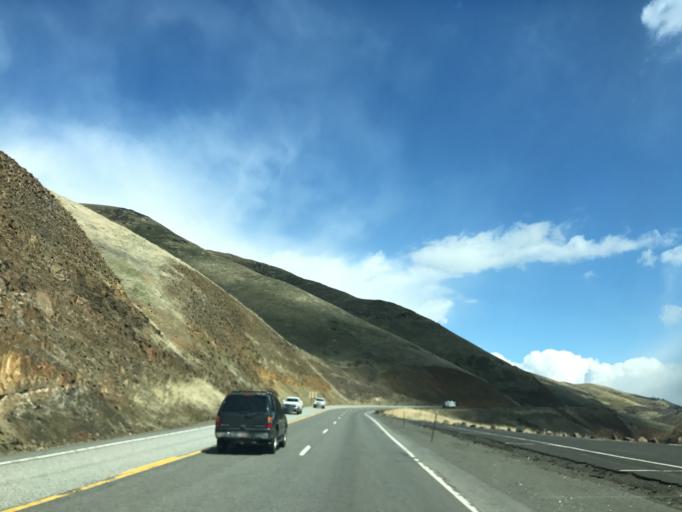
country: US
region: Idaho
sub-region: Idaho County
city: Grangeville
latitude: 45.8016
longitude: -116.2878
